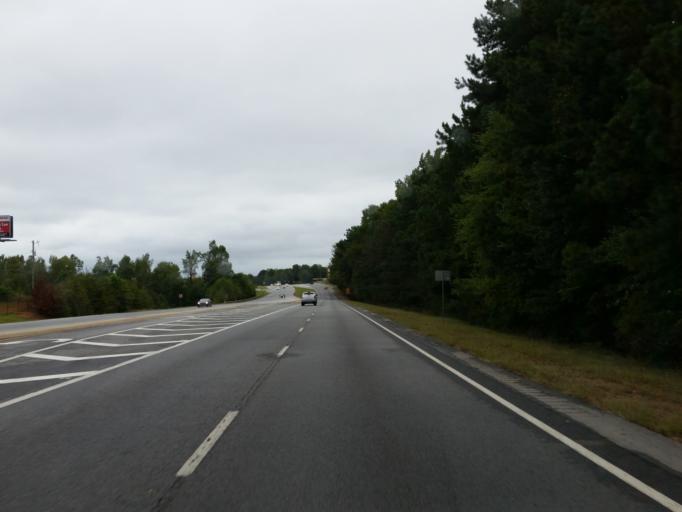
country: US
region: Georgia
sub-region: Henry County
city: Hampton
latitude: 33.4003
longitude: -84.3123
